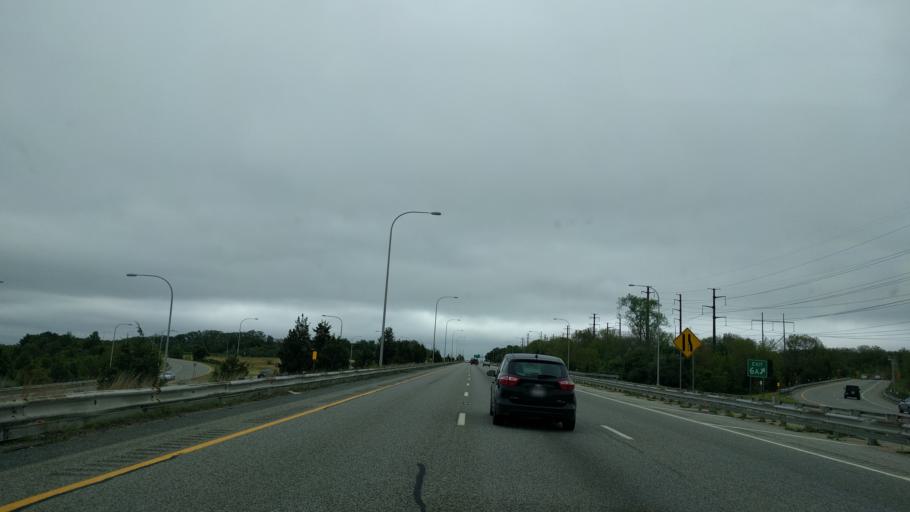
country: US
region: Rhode Island
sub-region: Providence County
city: Johnston
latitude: 41.8254
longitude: -71.5155
